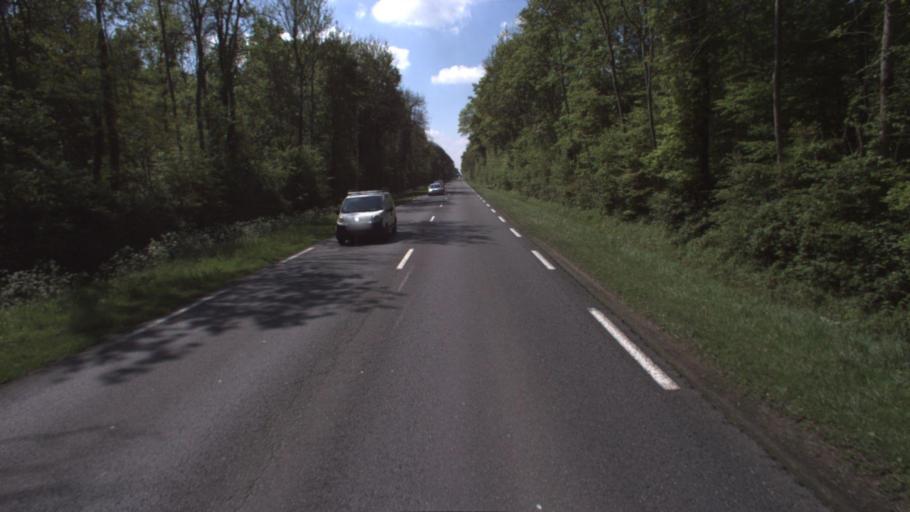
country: FR
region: Ile-de-France
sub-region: Departement de Seine-et-Marne
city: Villeneuve-le-Comte
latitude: 48.8102
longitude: 2.8740
